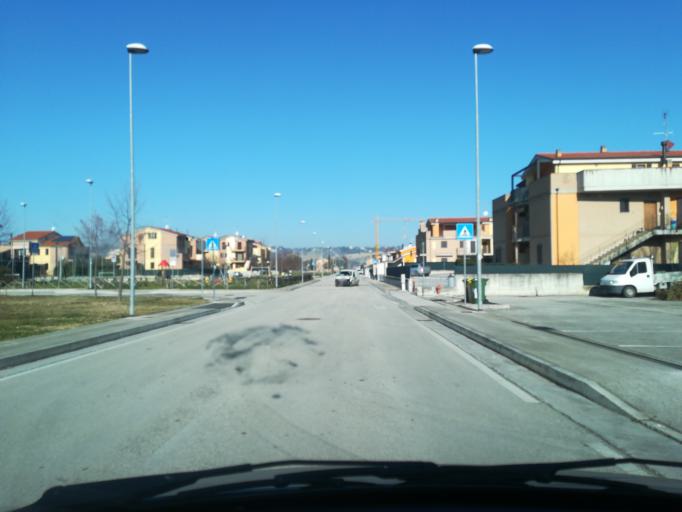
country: IT
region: The Marches
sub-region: Provincia di Macerata
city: Zona Industriale
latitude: 43.2606
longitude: 13.4971
